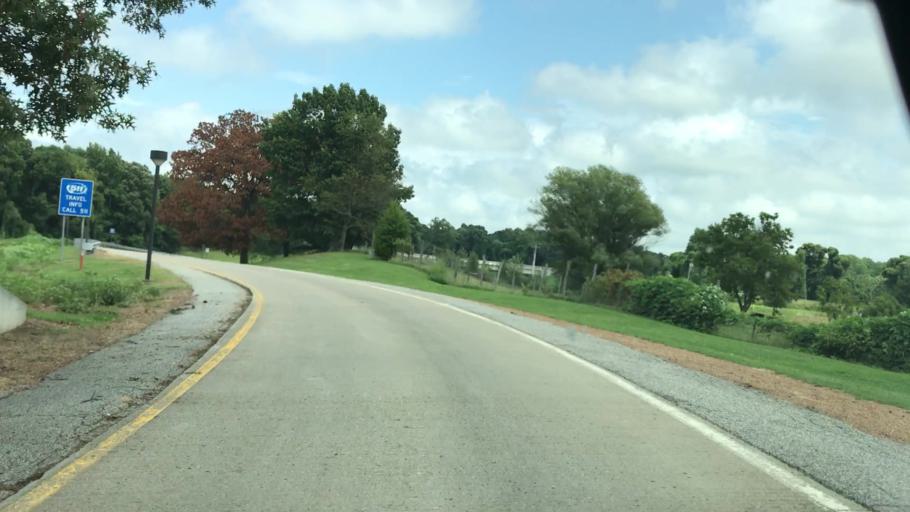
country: US
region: Tennessee
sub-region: Dyer County
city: Dyersburg
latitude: 36.0703
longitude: -89.4668
